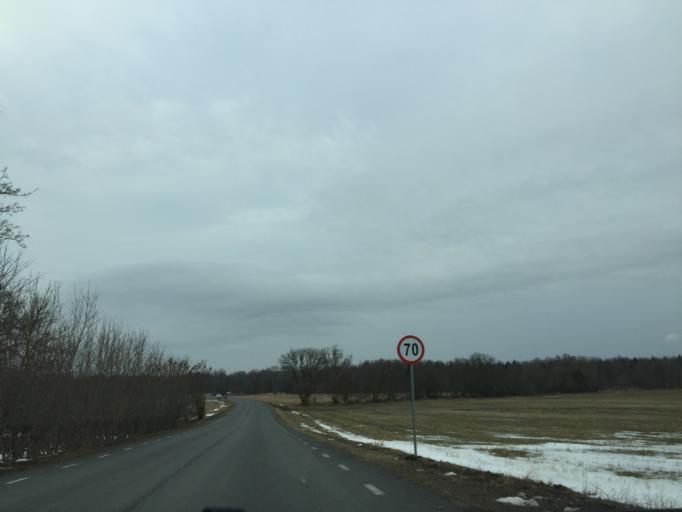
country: EE
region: Saare
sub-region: Kuressaare linn
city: Kuressaare
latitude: 58.4624
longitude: 22.2373
